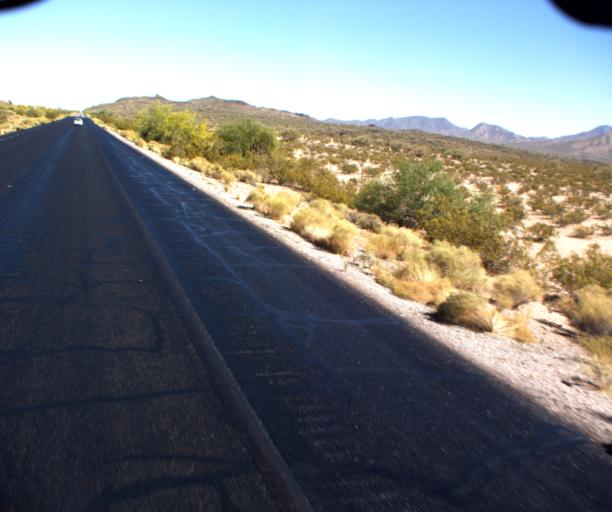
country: US
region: Arizona
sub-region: Pinal County
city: Maricopa
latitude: 32.8364
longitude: -112.2079
